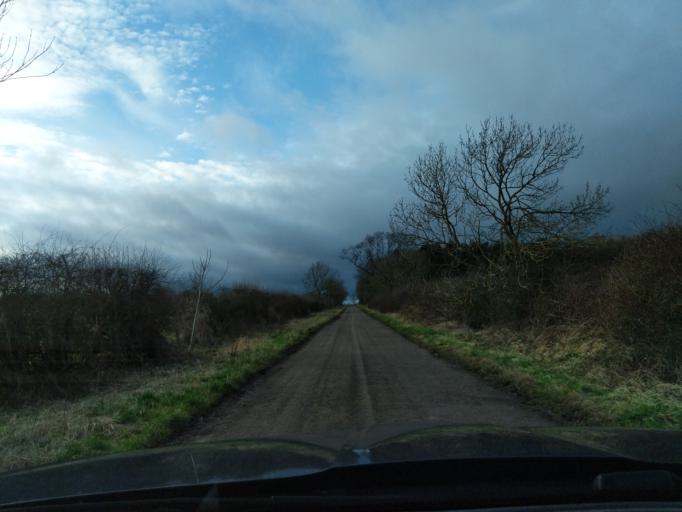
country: GB
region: England
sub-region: Northumberland
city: Ancroft
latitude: 55.6851
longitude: -1.9661
